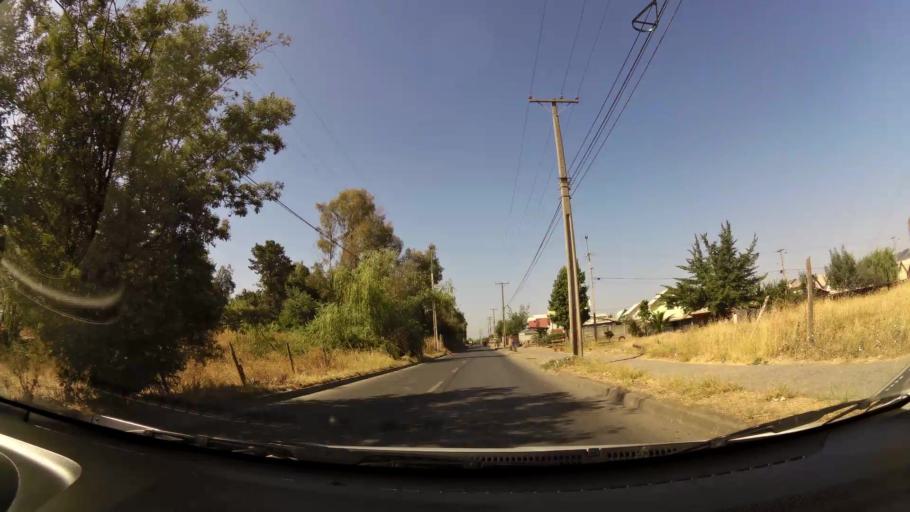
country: CL
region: Maule
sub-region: Provincia de Talca
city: Talca
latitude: -35.3981
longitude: -71.6518
